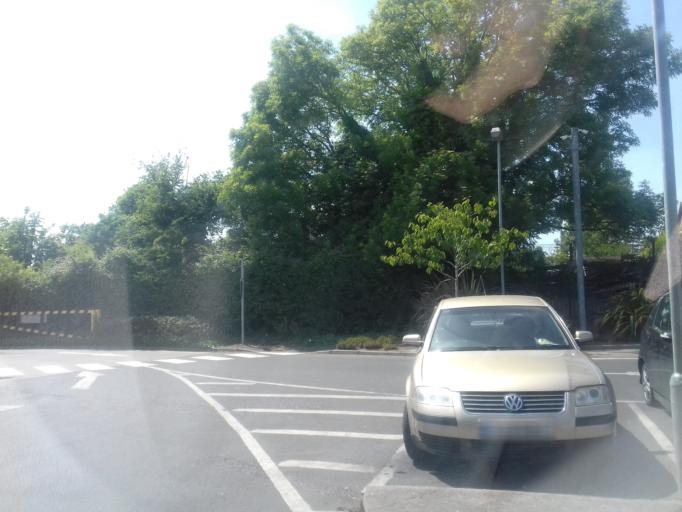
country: IE
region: Leinster
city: Lusk
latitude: 53.5266
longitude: -6.1640
